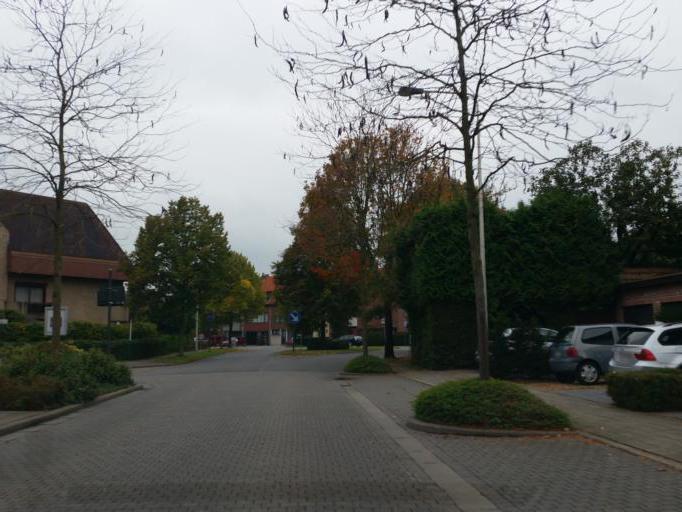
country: BE
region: Flanders
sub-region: Provincie Antwerpen
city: Edegem
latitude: 51.1498
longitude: 4.4511
